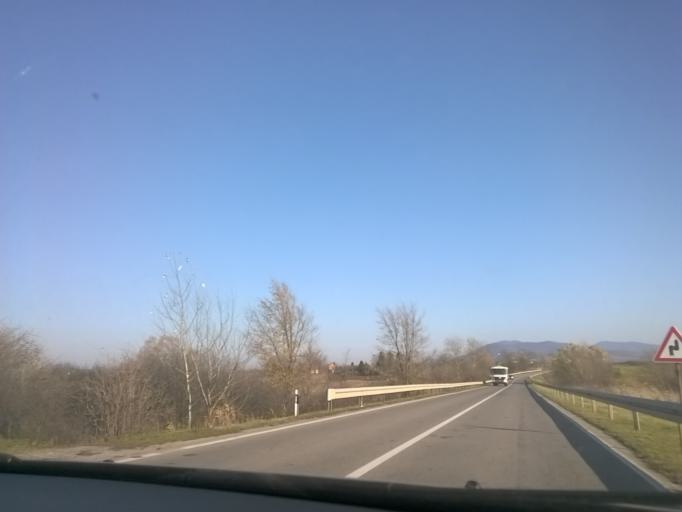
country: RS
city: Pavlis
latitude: 45.0867
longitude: 21.2457
